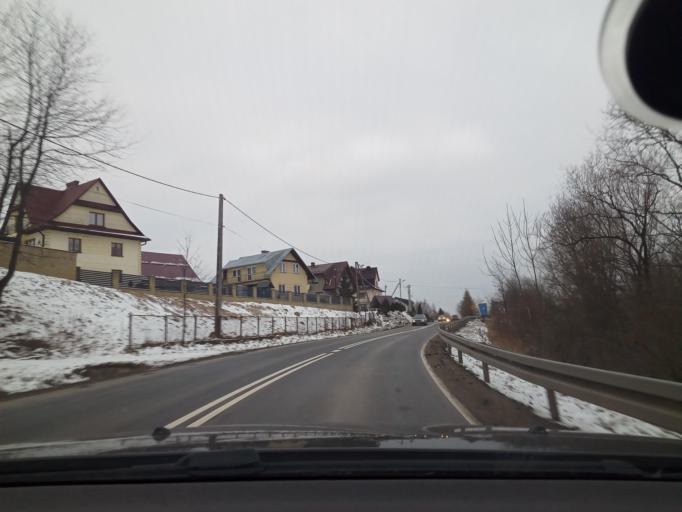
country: PL
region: Lesser Poland Voivodeship
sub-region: Powiat limanowski
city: Lubomierz
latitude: 49.6200
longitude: 20.1549
